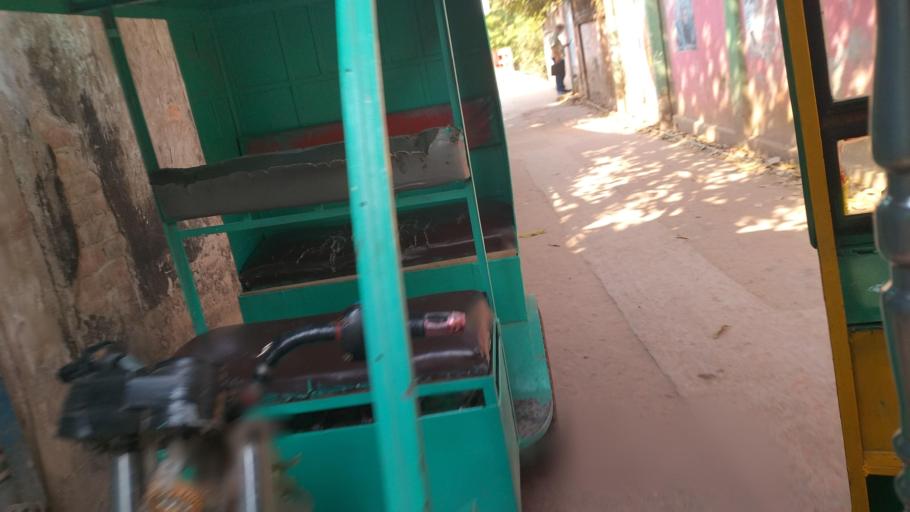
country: BD
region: Dhaka
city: Azimpur
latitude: 23.7956
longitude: 90.3373
